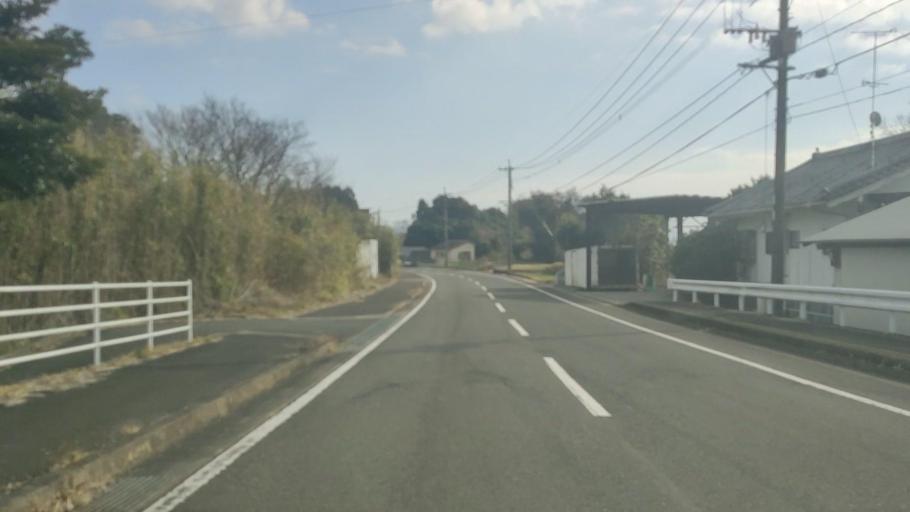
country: JP
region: Nagasaki
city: Shimabara
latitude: 32.6805
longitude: 130.2766
